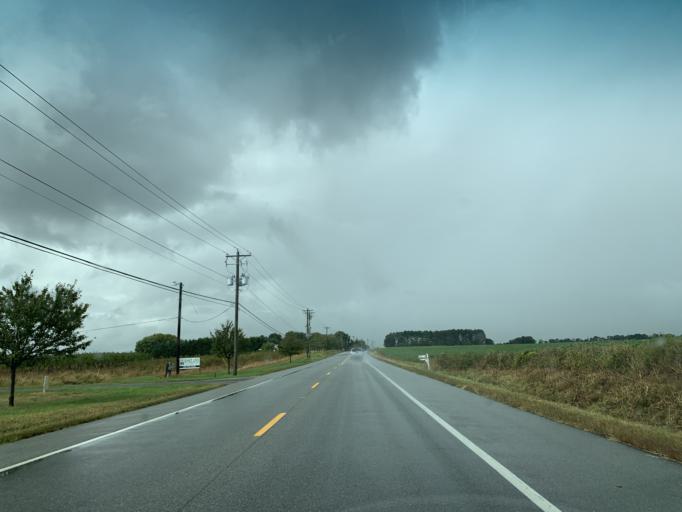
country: US
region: Maryland
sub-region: Queen Anne's County
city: Kingstown
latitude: 39.1962
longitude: -75.8615
